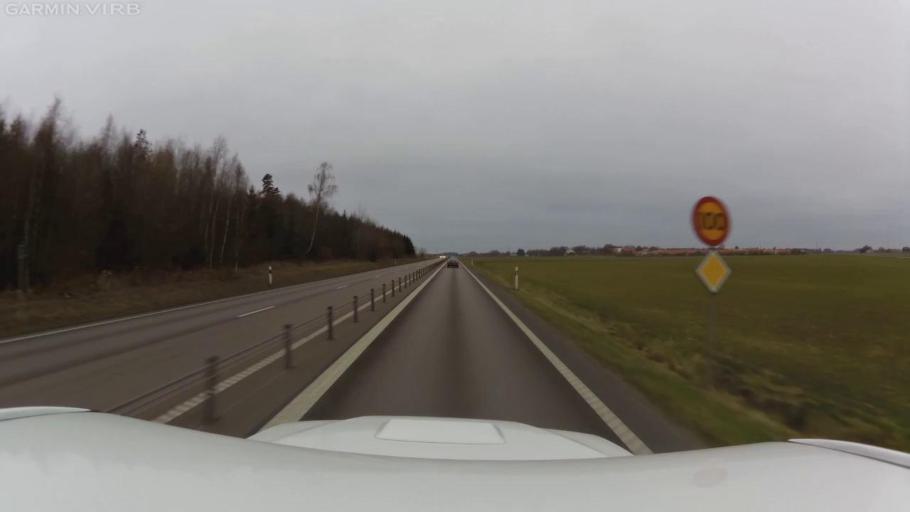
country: SE
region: OEstergoetland
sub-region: Linkopings Kommun
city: Vikingstad
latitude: 58.3759
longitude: 15.4551
